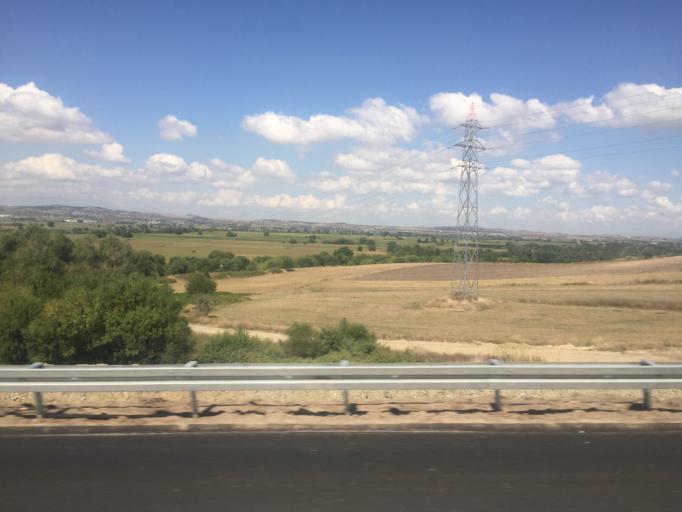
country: TR
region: Balikesir
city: Gobel
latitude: 40.0339
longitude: 28.2148
